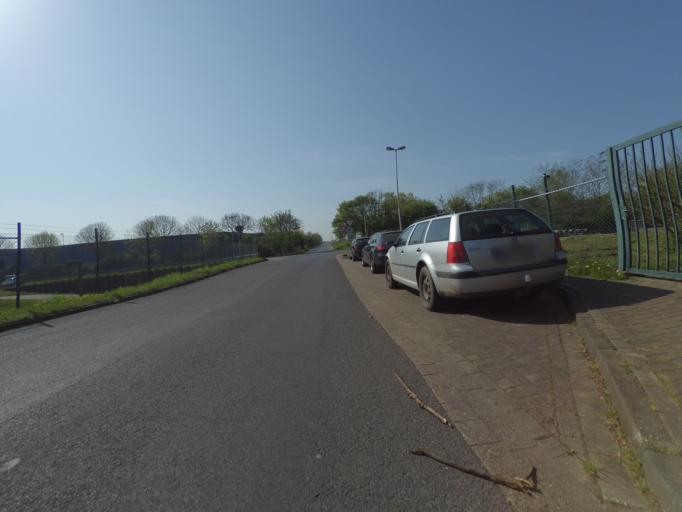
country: DE
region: North Rhine-Westphalia
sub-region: Regierungsbezirk Dusseldorf
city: Emmerich
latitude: 51.8297
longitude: 6.2707
